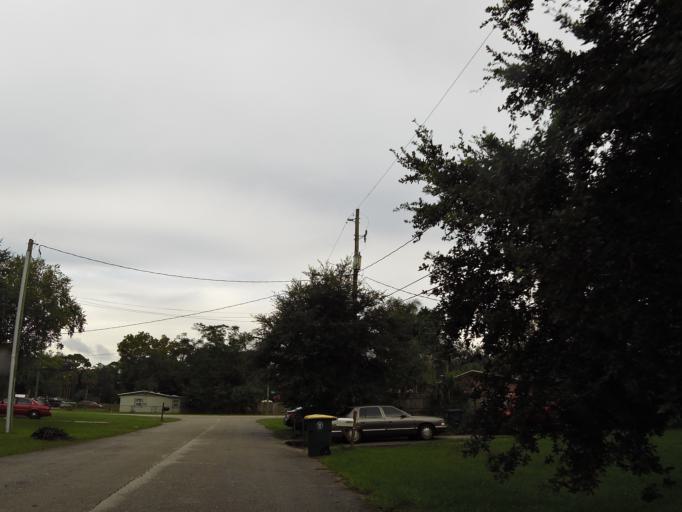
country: US
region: Florida
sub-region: Duval County
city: Neptune Beach
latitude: 30.2915
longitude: -81.5019
